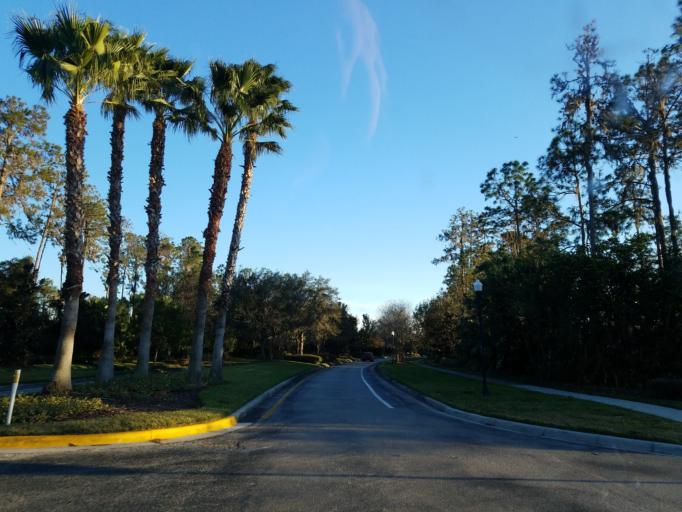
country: US
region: Florida
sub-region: Pasco County
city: Wesley Chapel
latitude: 28.2046
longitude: -82.3669
